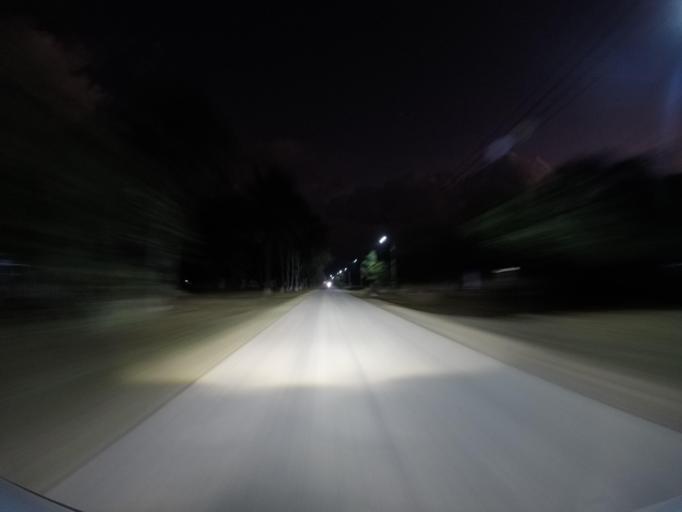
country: TL
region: Lautem
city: Lospalos
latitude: -8.4721
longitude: 126.9930
